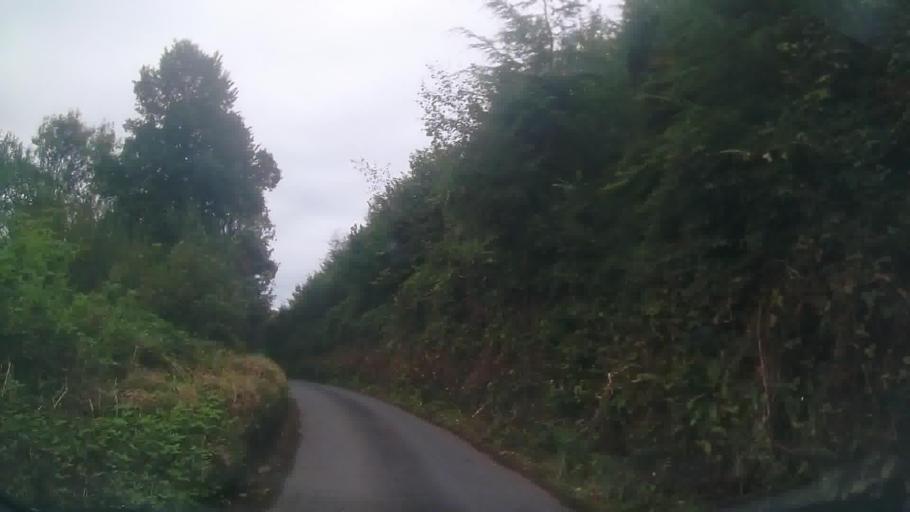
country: GB
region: Wales
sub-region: Pembrokeshire
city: Saundersfoot
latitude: 51.7382
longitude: -4.6604
